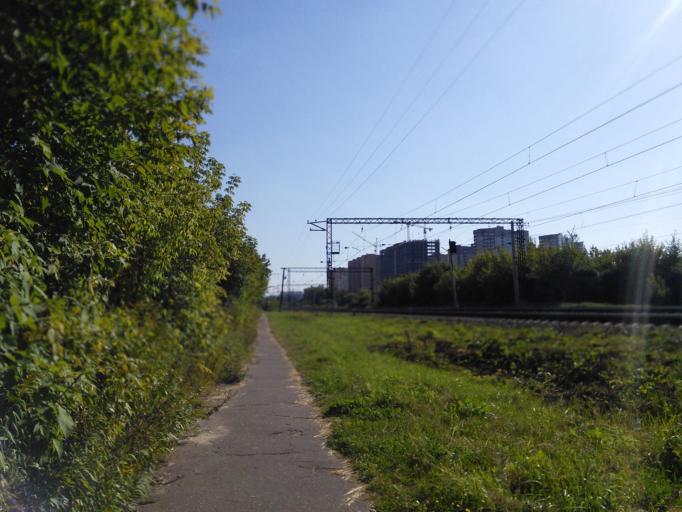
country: RU
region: Moskovskaya
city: Shcherbinka
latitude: 55.4993
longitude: 37.5594
